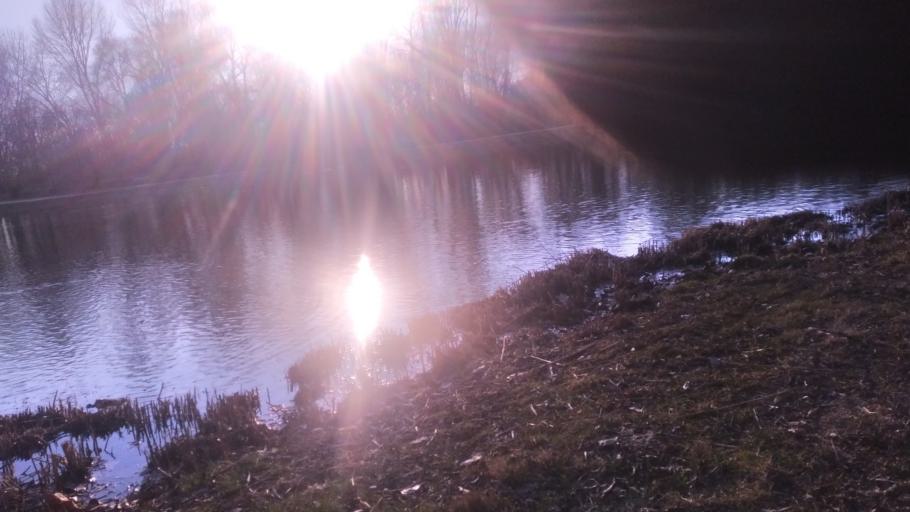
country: HU
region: Komarom-Esztergom
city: Tatabanya
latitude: 47.5776
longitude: 18.3993
